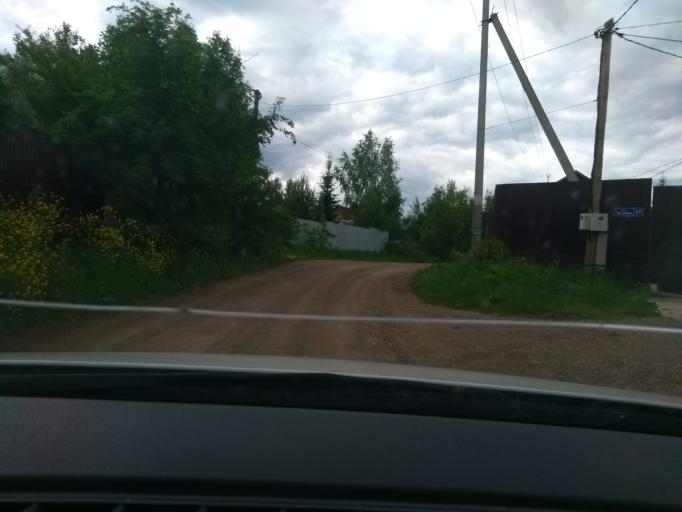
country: RU
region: Perm
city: Sylva
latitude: 57.8445
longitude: 56.7974
